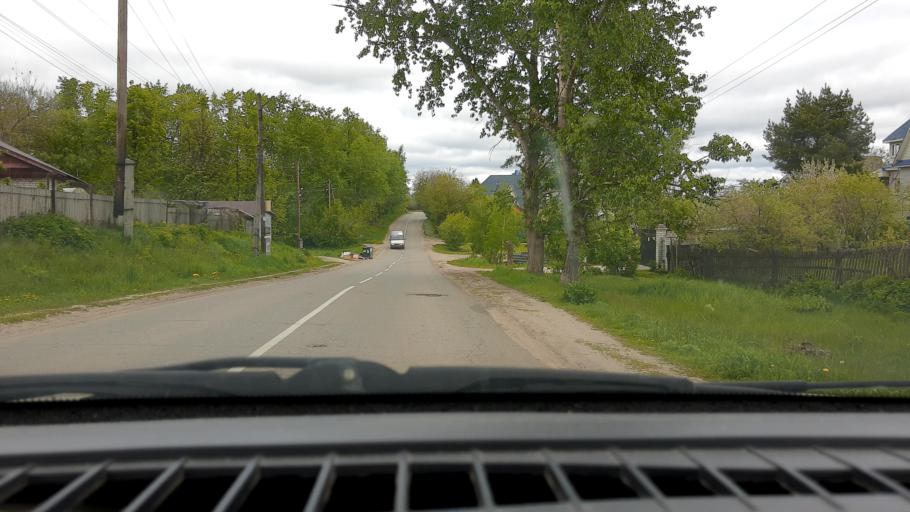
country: RU
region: Nizjnij Novgorod
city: Lukino
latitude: 56.4097
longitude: 43.7133
